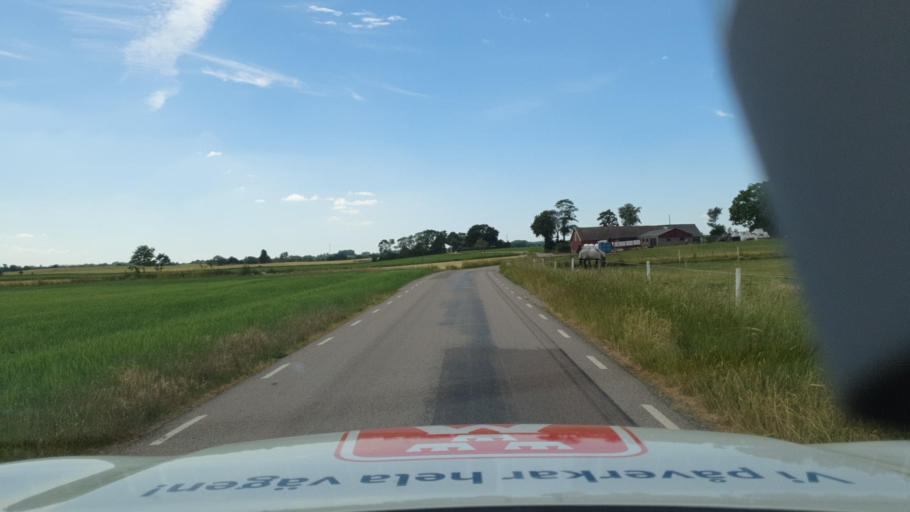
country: SE
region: Skane
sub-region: Sjobo Kommun
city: Sjoebo
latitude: 55.6358
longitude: 13.8069
